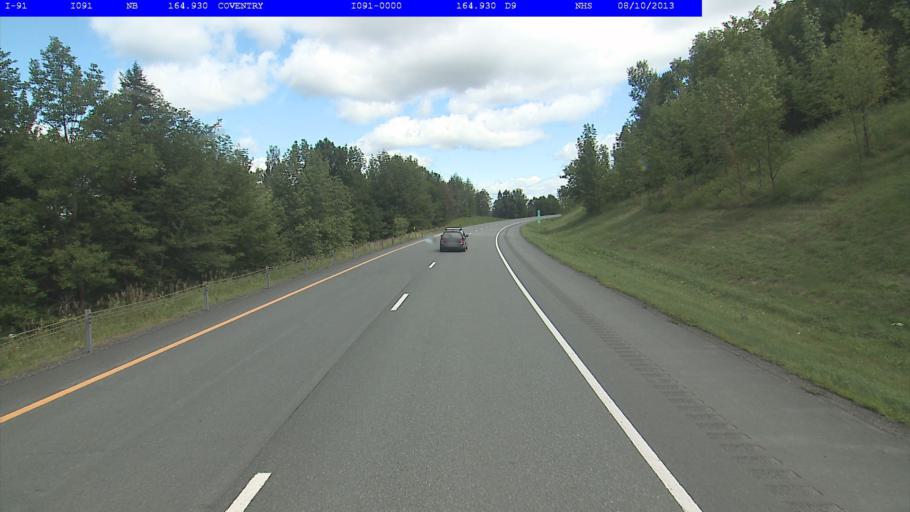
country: US
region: Vermont
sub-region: Orleans County
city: Newport
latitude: 44.8536
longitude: -72.1932
